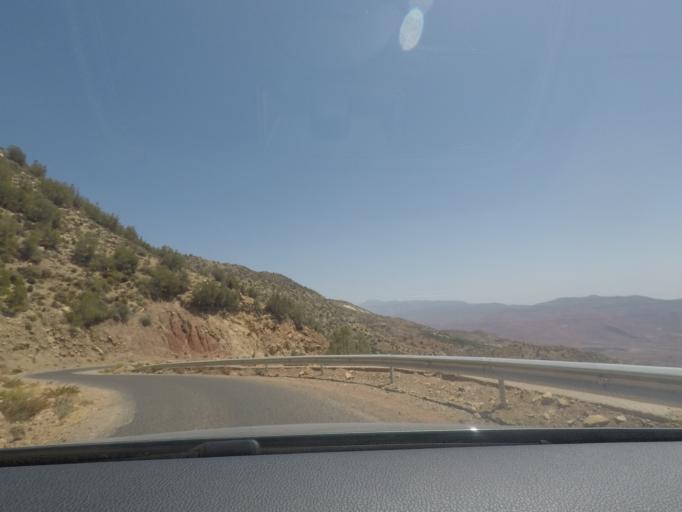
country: MA
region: Souss-Massa-Draa
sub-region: Taroudannt
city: Bigoudine
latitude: 30.7462
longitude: -9.2806
